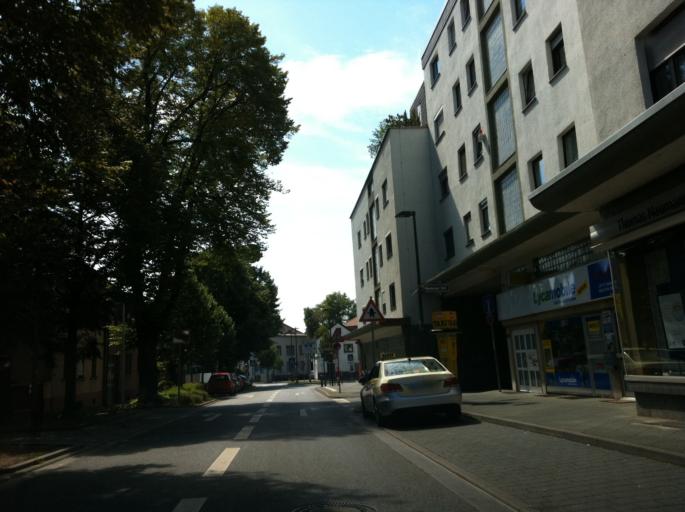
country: DE
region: Hesse
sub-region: Regierungsbezirk Darmstadt
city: Bad Homburg vor der Hoehe
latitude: 50.1841
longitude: 8.6651
